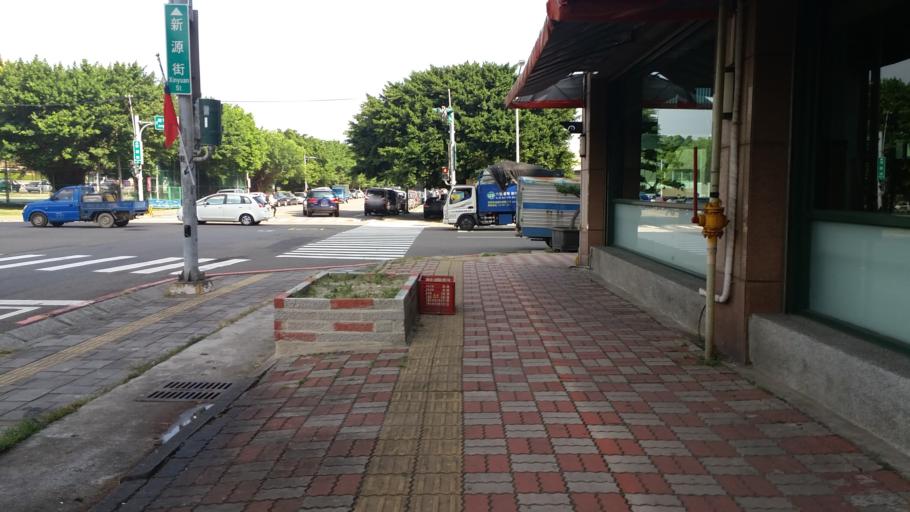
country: TW
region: Taiwan
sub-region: Hsinchu
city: Hsinchu
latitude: 24.8027
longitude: 120.9934
